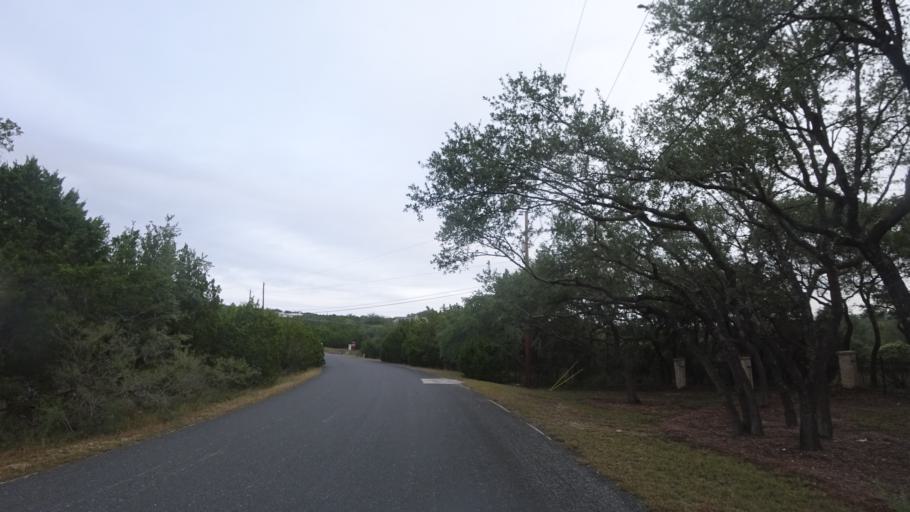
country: US
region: Texas
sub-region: Travis County
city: Hudson Bend
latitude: 30.3886
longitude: -97.9172
